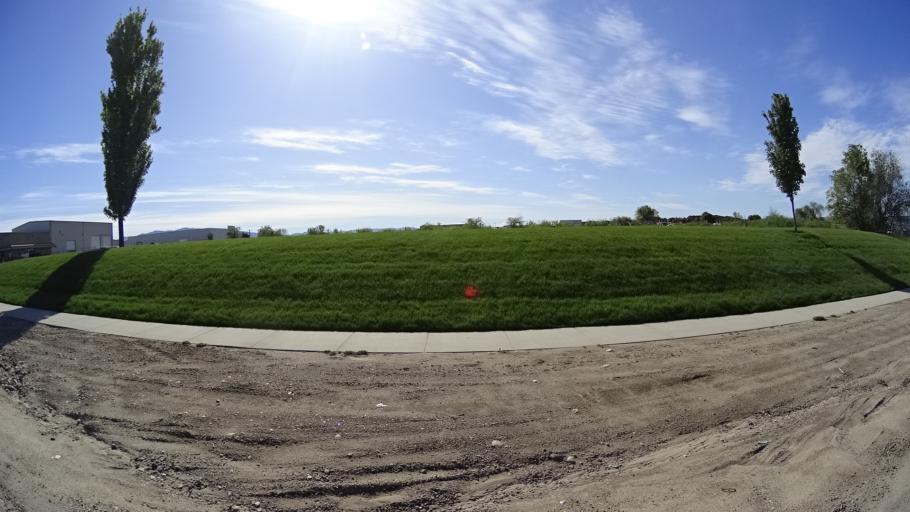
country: US
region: Idaho
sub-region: Ada County
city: Garden City
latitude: 43.5693
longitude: -116.2594
